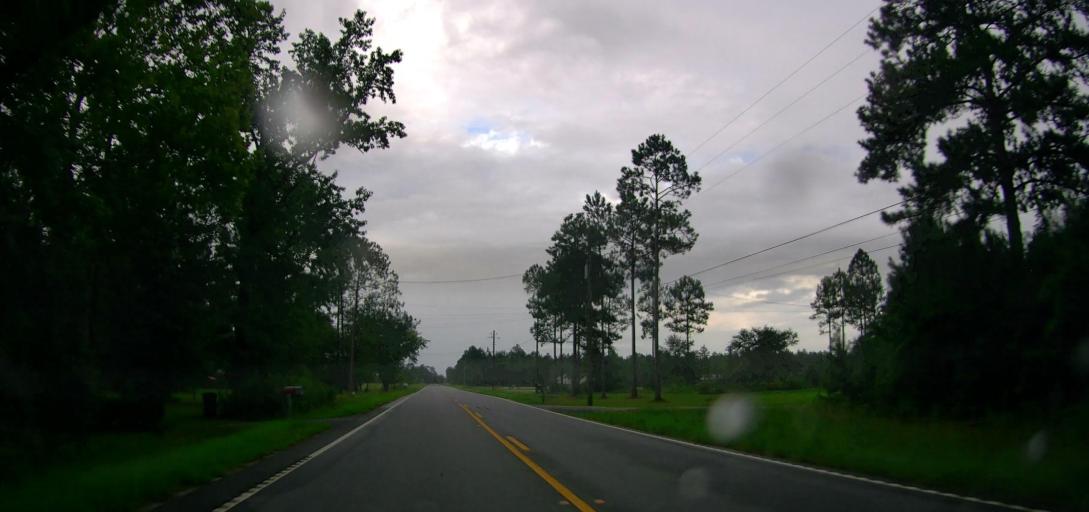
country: US
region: Georgia
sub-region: Ware County
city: Deenwood
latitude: 31.2875
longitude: -82.4409
